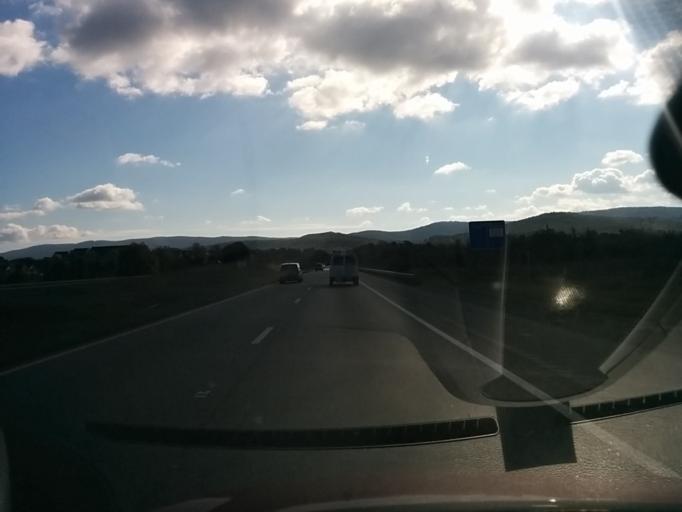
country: US
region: Virginia
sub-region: Augusta County
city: Lyndhurst
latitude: 38.0583
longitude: -78.9327
